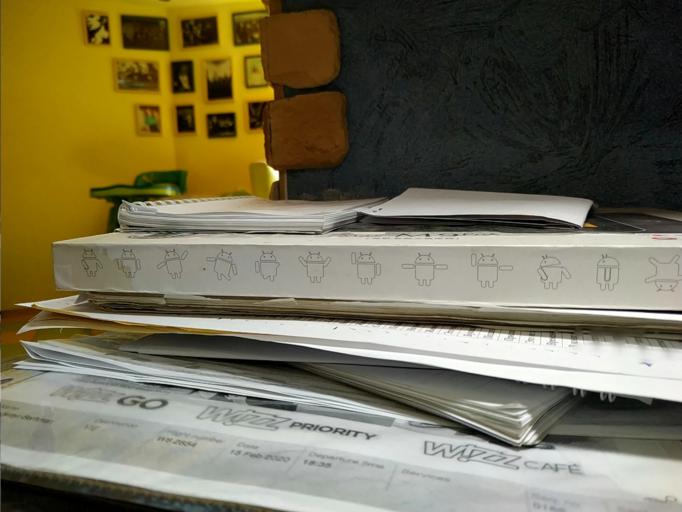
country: RU
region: Novgorod
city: Sol'tsy
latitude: 58.1075
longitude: 30.1003
